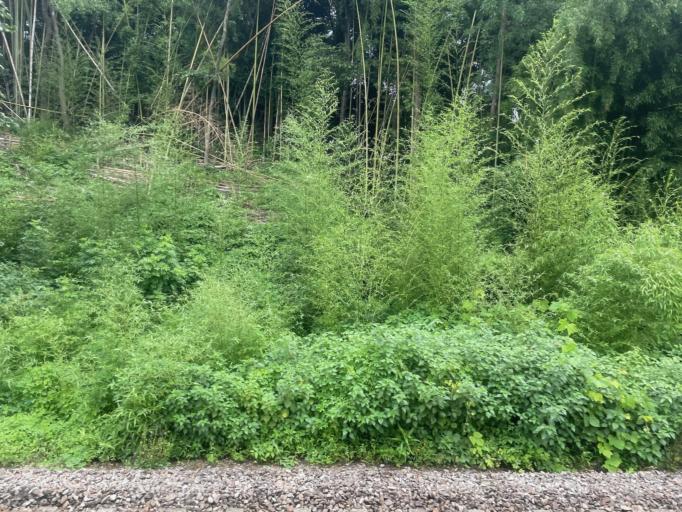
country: JP
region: Gunma
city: Shibukawa
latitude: 36.5415
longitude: 139.0333
